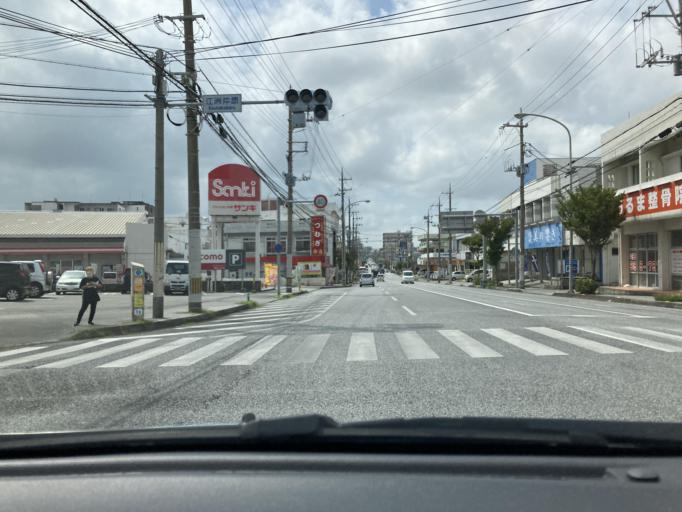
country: JP
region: Okinawa
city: Okinawa
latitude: 26.3522
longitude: 127.8281
